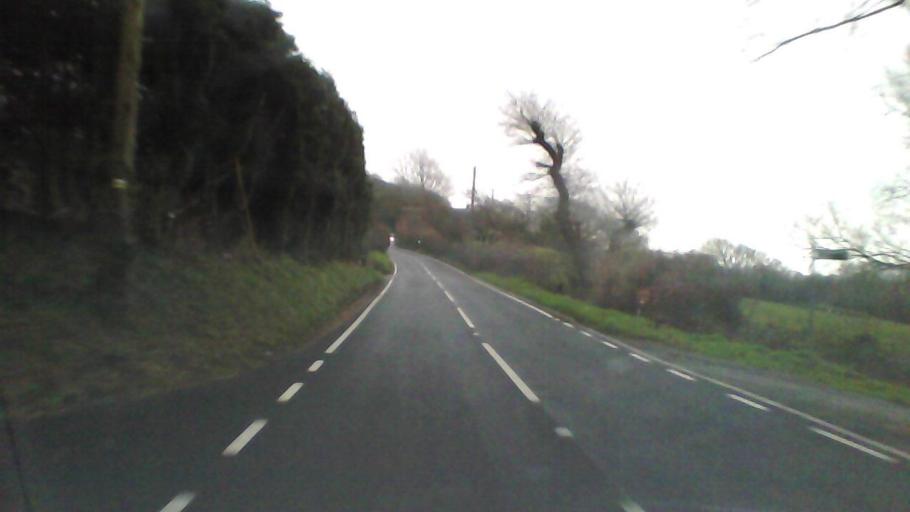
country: GB
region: England
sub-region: Isle of Wight
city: Newport
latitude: 50.6942
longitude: -1.2610
